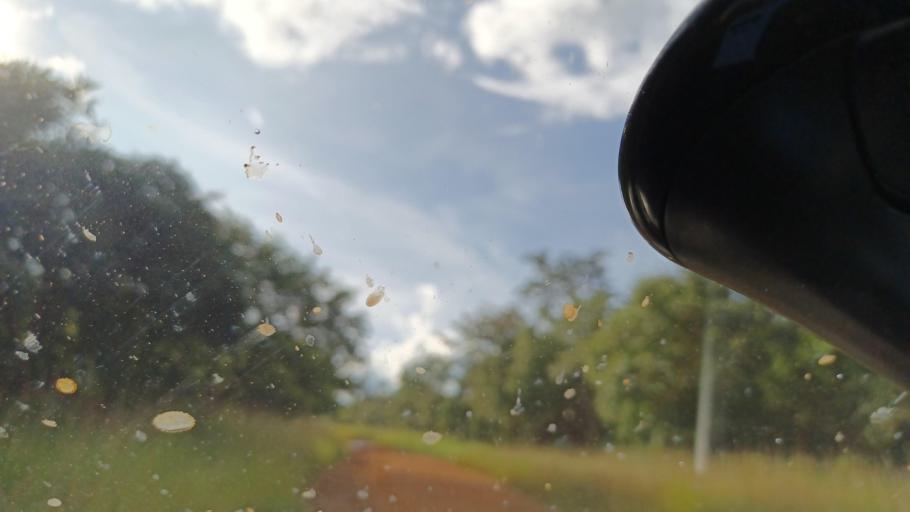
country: ZM
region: North-Western
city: Kasempa
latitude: -13.6270
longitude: 26.2160
